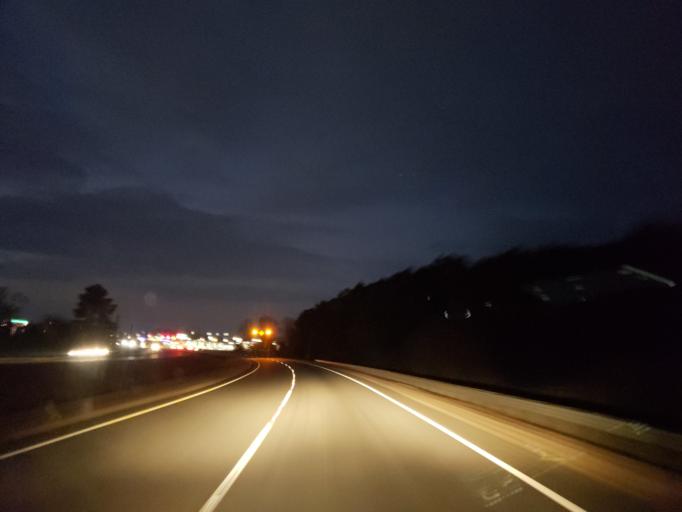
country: US
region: Georgia
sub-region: Polk County
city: Rockmart
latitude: 34.0059
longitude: -85.0263
